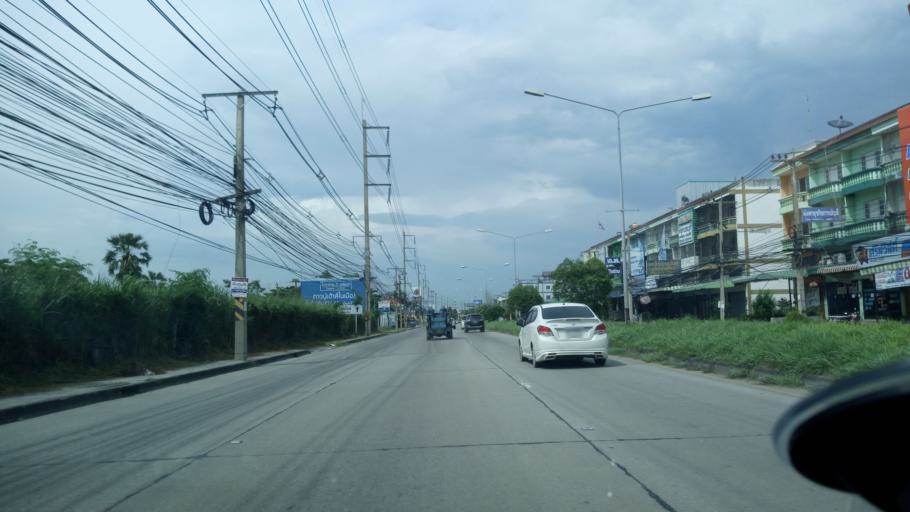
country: TH
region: Chon Buri
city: Chon Buri
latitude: 13.3983
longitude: 101.0262
